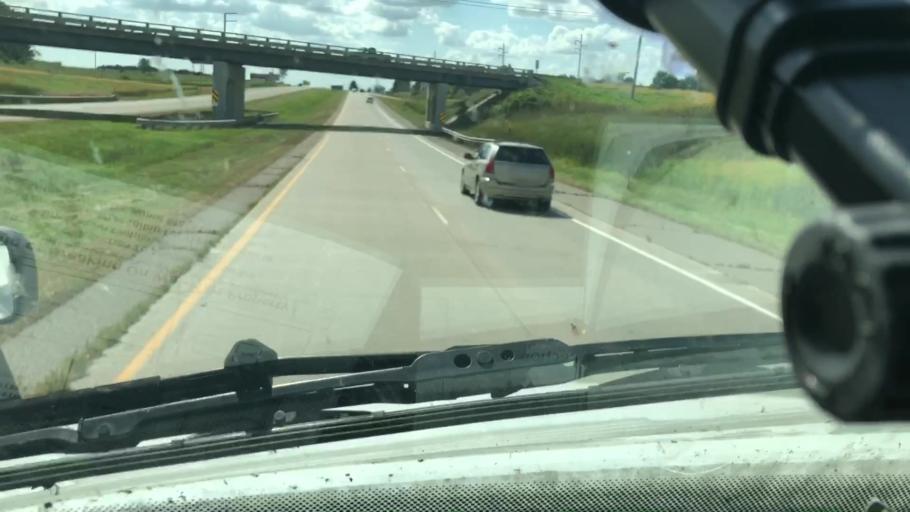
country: US
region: Minnesota
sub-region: Mower County
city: Austin
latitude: 43.6673
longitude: -93.0204
